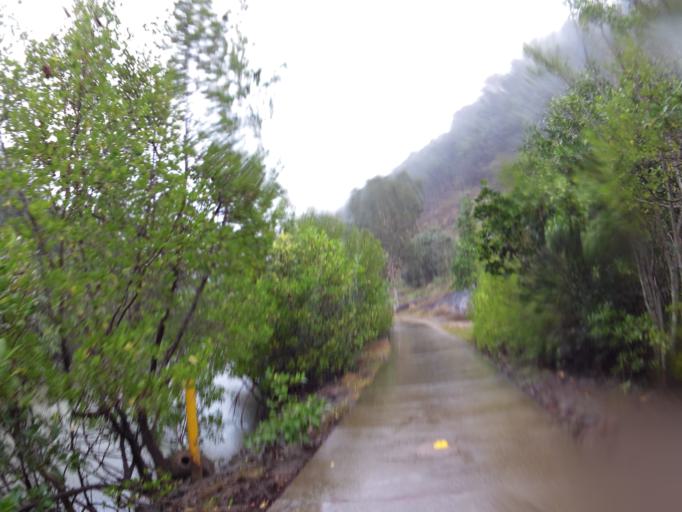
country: AU
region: Queensland
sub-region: Cairns
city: Cairns
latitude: -16.8940
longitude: 145.7523
